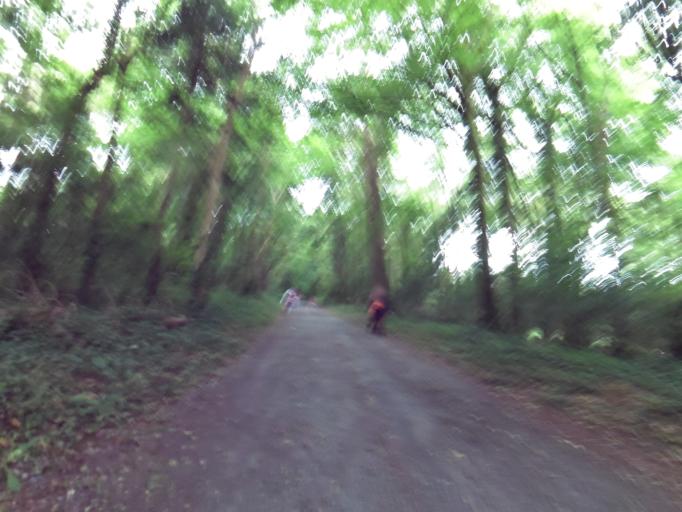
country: IE
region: Connaught
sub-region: County Galway
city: Gort
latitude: 53.0803
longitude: -8.8714
